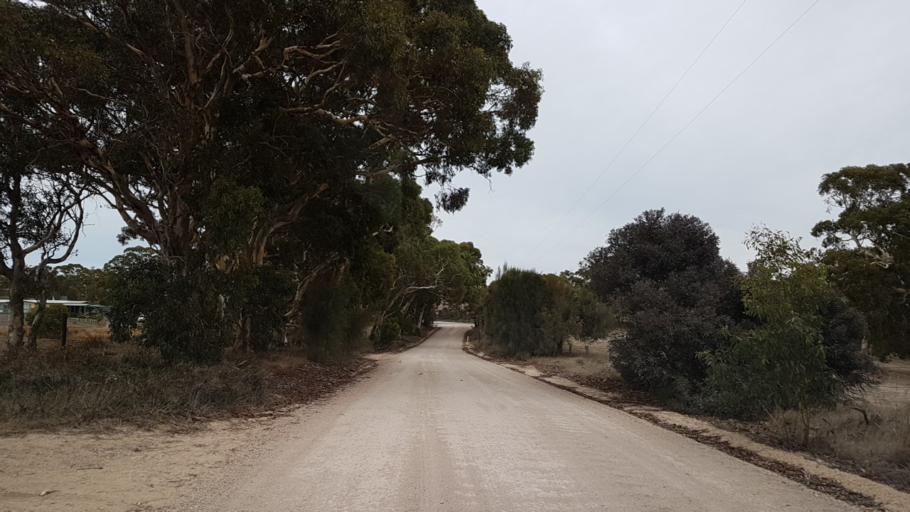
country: AU
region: South Australia
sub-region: Mount Barker
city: Nairne
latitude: -34.9979
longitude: 138.9737
